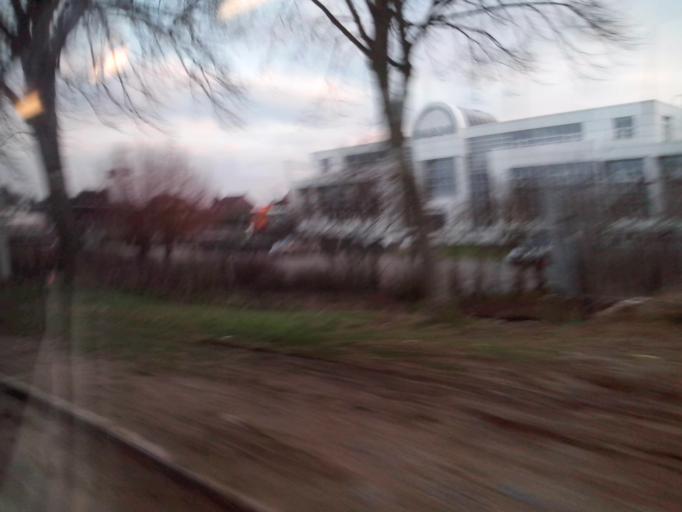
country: BE
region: Flanders
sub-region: Provincie Vlaams-Brabant
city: Asse
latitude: 50.8954
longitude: 4.2404
